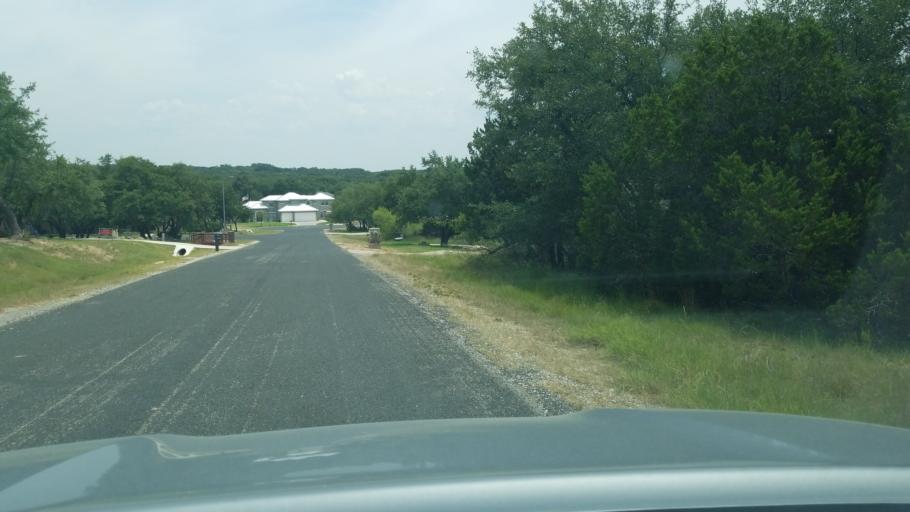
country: US
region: Texas
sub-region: Bexar County
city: Timberwood Park
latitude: 29.6893
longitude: -98.5071
